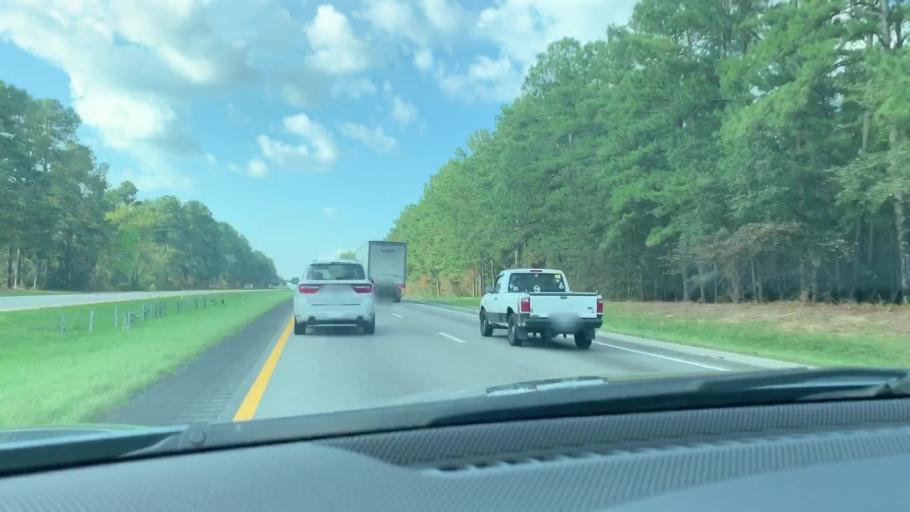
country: US
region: South Carolina
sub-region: Calhoun County
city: Oak Grove
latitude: 33.6951
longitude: -80.9126
